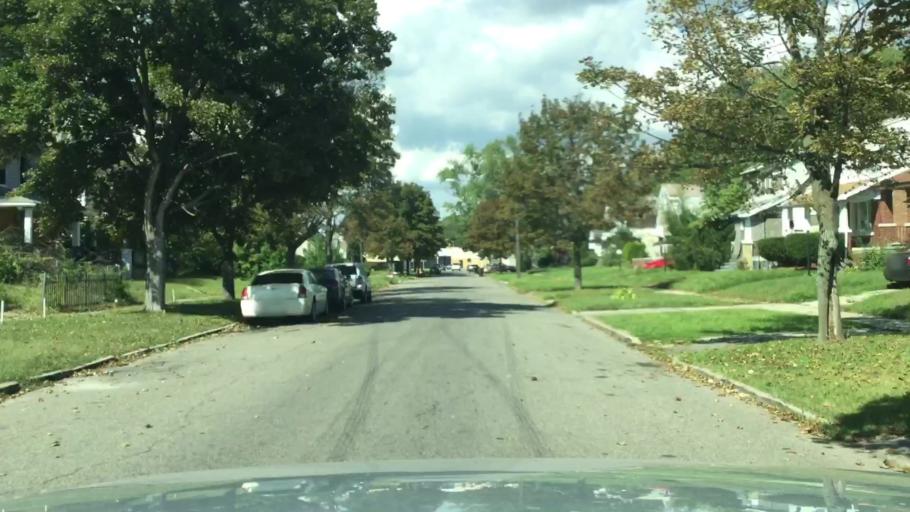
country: US
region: Michigan
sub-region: Wayne County
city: Highland Park
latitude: 42.4306
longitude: -83.0889
